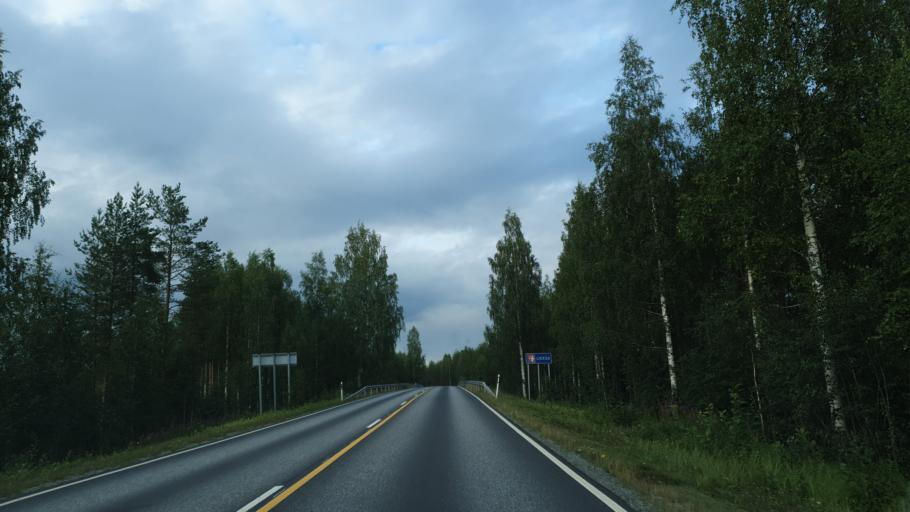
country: FI
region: North Karelia
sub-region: Joensuu
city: Eno
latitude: 63.0374
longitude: 30.1131
